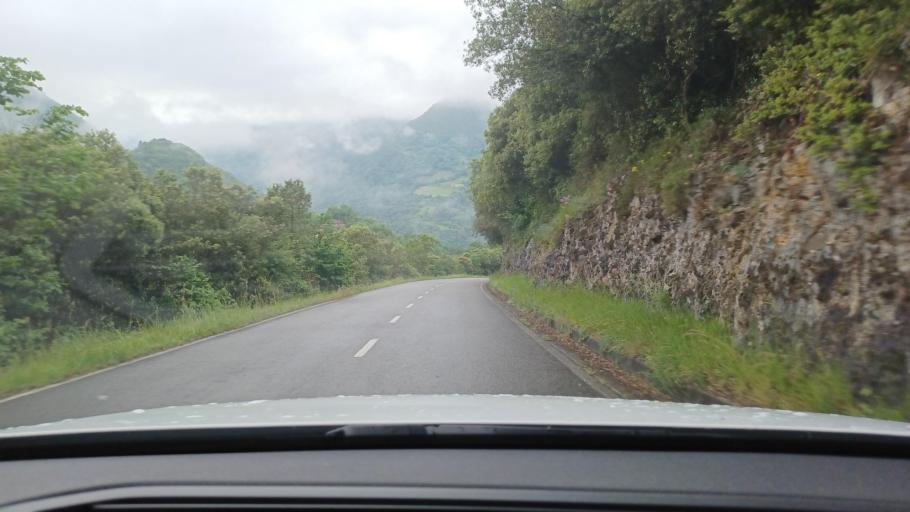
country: ES
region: Asturias
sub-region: Province of Asturias
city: Proaza
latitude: 43.2897
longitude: -5.9723
